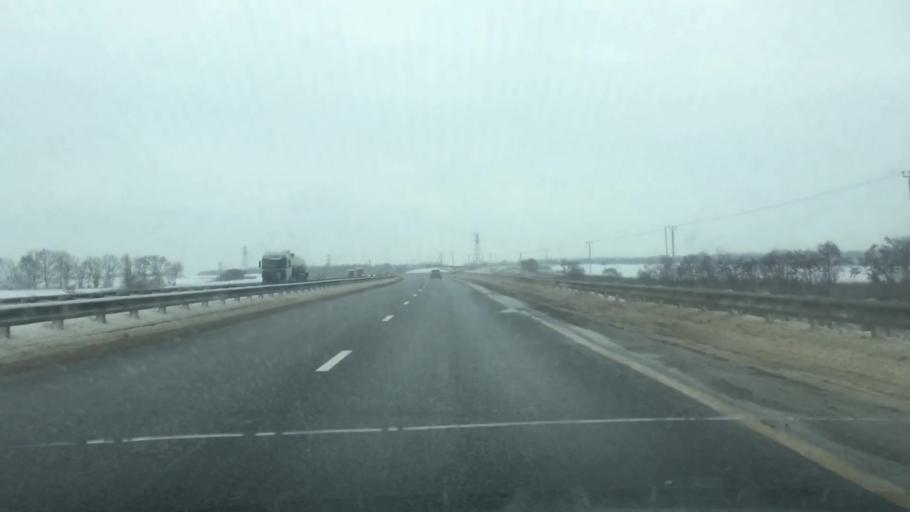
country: RU
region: Tula
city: Yefremov
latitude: 53.1027
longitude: 38.1786
